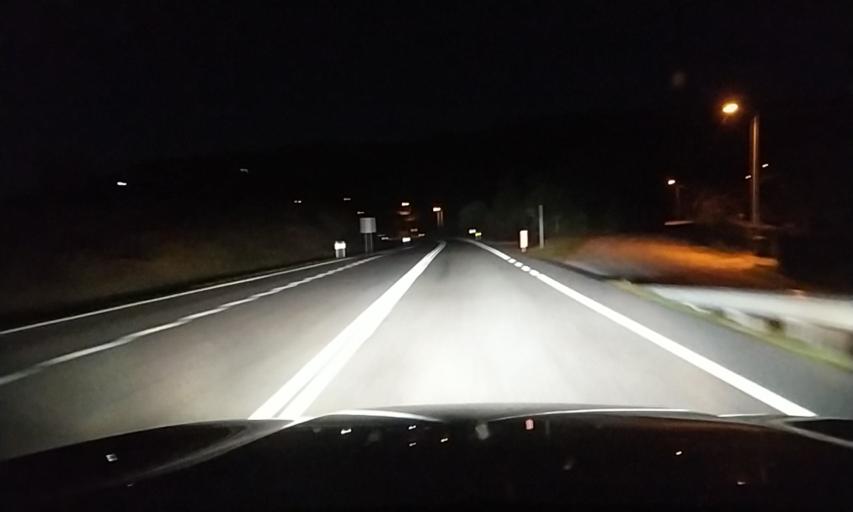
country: ES
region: Galicia
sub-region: Provincia de Ourense
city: Cualedro
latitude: 41.9720
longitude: -7.5200
